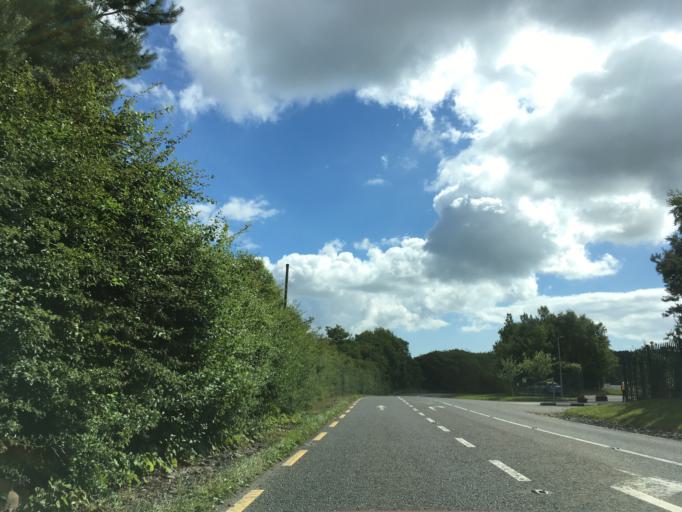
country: IE
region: Munster
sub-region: County Cork
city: Carrigaline
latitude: 51.8109
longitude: -8.3665
